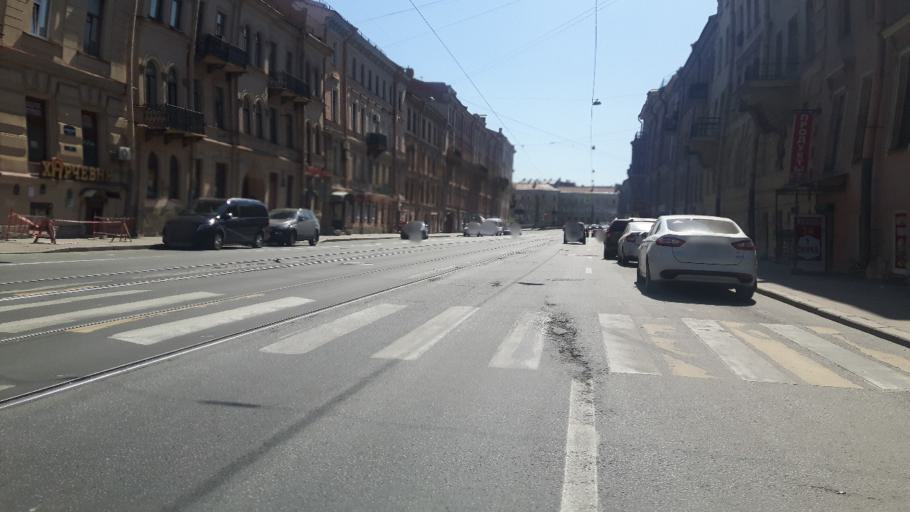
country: RU
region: St.-Petersburg
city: Admiralteisky
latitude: 59.9188
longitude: 30.2958
